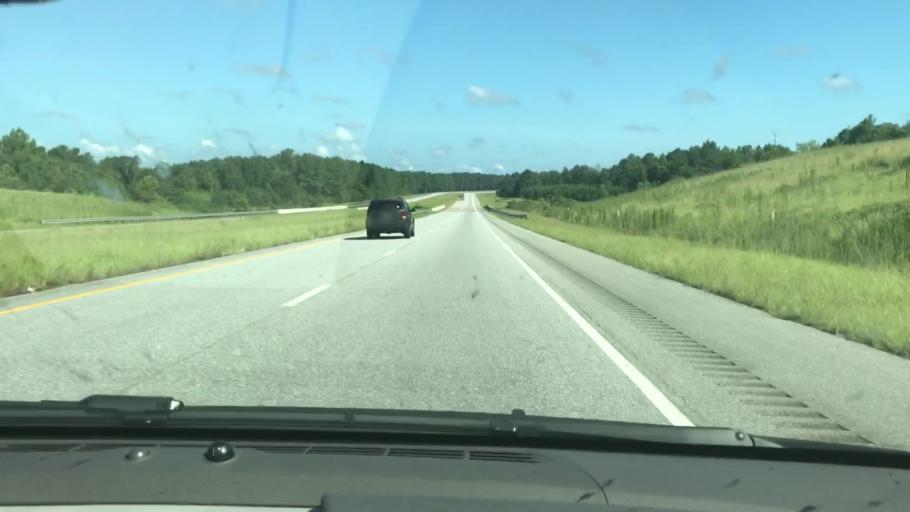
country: US
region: Alabama
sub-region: Barbour County
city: Eufaula
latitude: 32.1798
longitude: -85.1787
